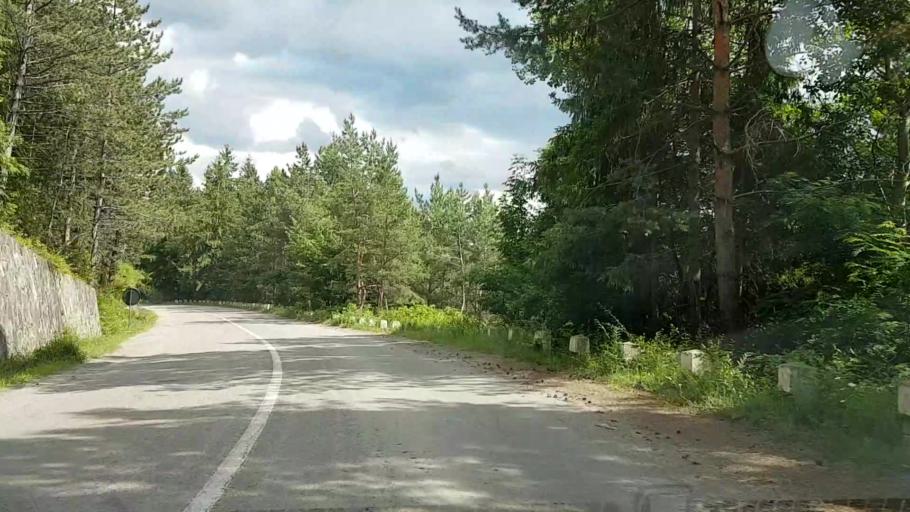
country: RO
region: Neamt
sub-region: Comuna Hangu
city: Hangu
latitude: 47.0494
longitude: 26.0086
